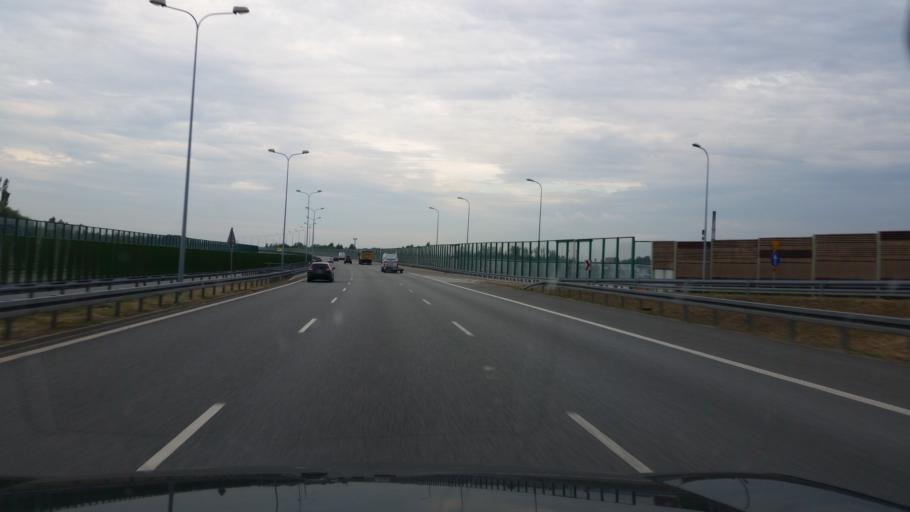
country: PL
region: Silesian Voivodeship
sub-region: Powiat gliwicki
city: Gieraltowice
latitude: 50.2242
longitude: 18.6934
